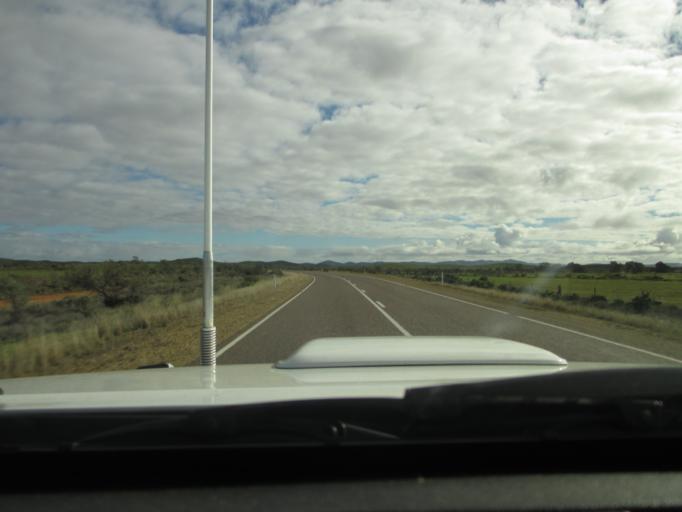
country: AU
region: South Australia
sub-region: Flinders Ranges
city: Quorn
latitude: -32.3417
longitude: 138.4834
